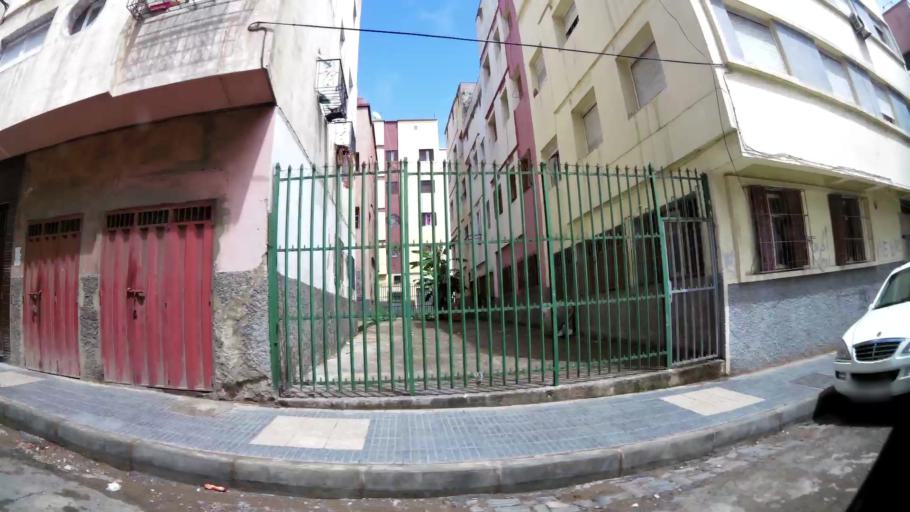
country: MA
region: Grand Casablanca
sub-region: Casablanca
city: Casablanca
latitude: 33.5735
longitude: -7.5833
